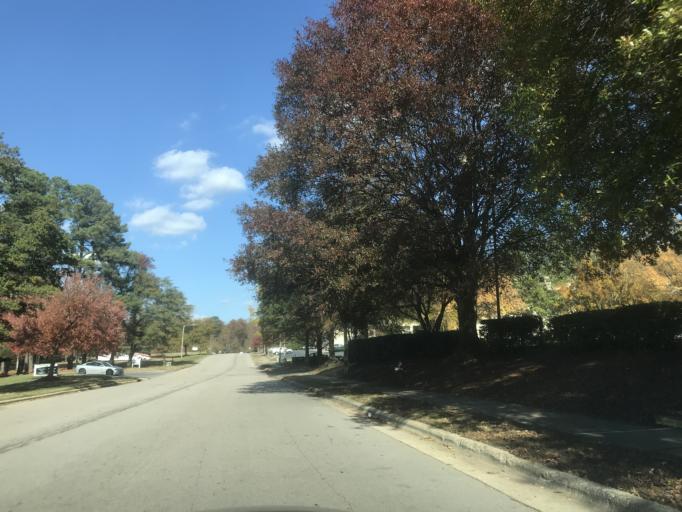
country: US
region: North Carolina
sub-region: Wake County
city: Raleigh
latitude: 35.8290
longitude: -78.6220
